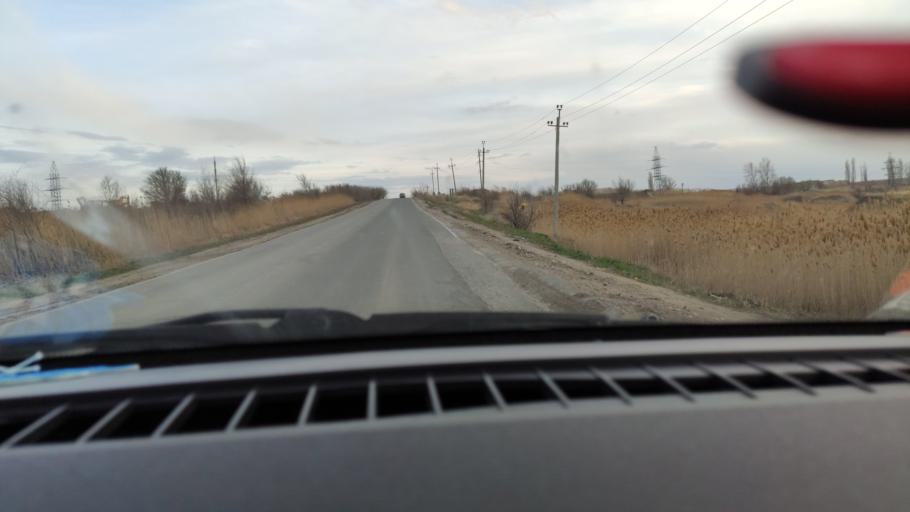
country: RU
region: Saratov
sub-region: Saratovskiy Rayon
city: Saratov
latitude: 51.6161
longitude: 45.9494
